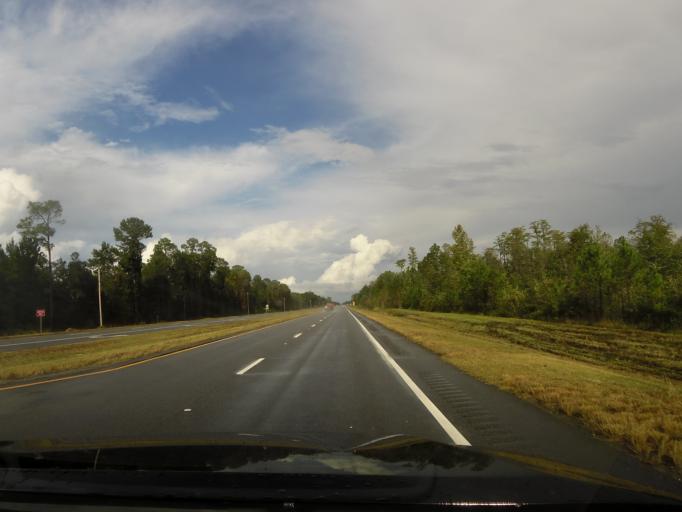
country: US
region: Georgia
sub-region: Liberty County
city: Walthourville
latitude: 31.7592
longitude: -81.6595
